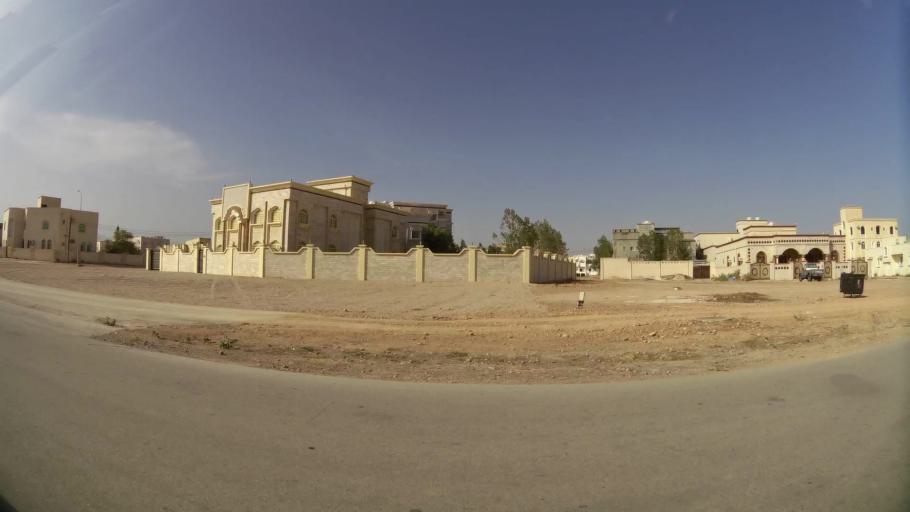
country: OM
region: Zufar
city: Salalah
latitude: 17.0077
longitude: 54.0151
